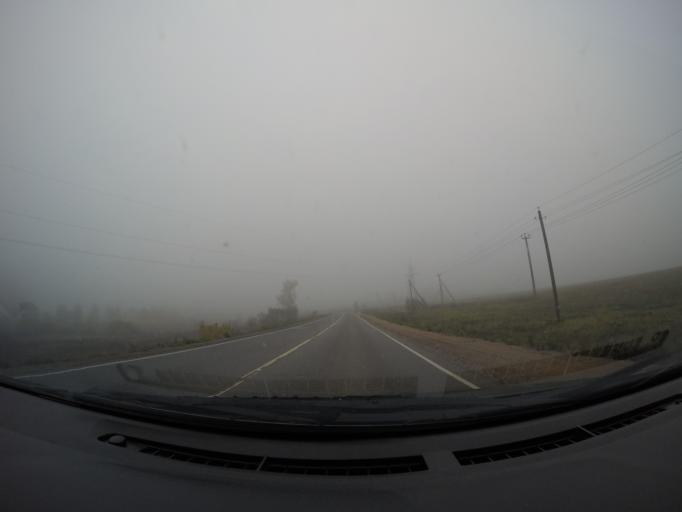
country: RU
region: Moskovskaya
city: Ruza
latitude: 55.7298
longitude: 36.3315
